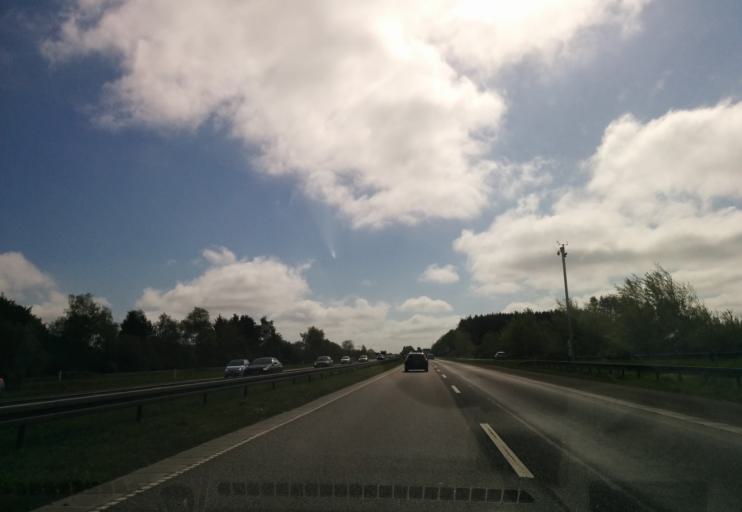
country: DK
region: South Denmark
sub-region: Assens Kommune
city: Vissenbjerg
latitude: 55.4004
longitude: 10.1587
